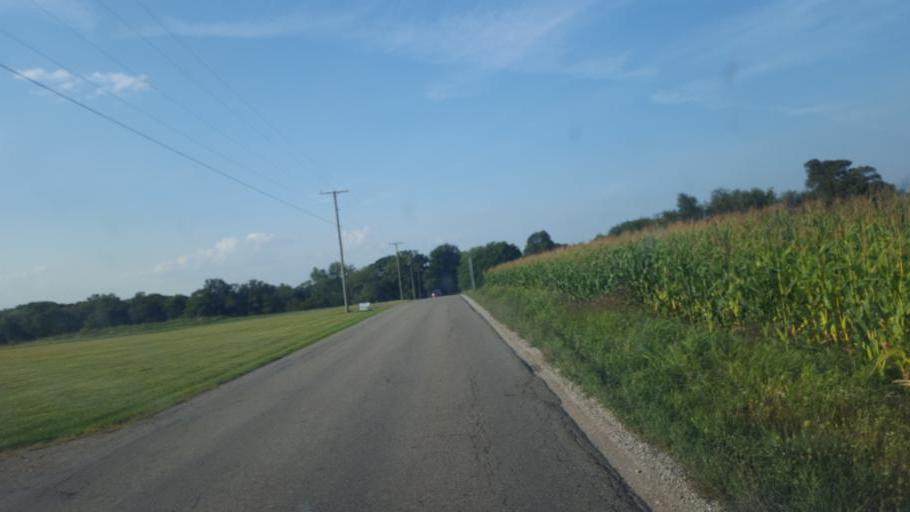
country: US
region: Ohio
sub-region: Knox County
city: Mount Vernon
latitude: 40.3887
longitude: -82.4453
